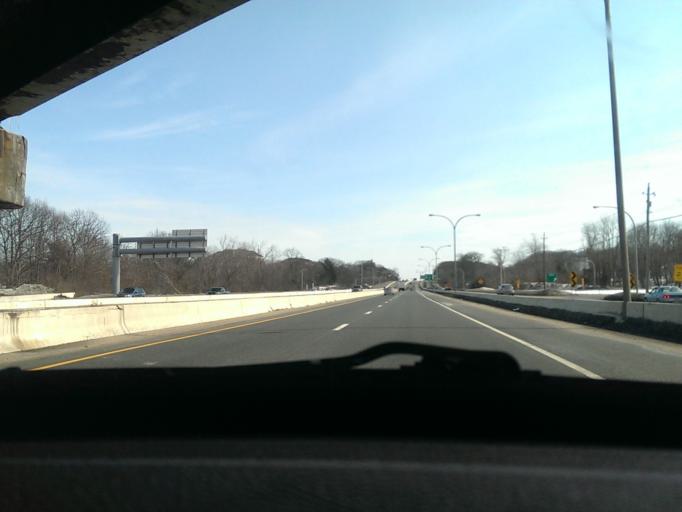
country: US
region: Rhode Island
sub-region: Providence County
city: Cumberland Hill
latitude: 41.9430
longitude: -71.4761
